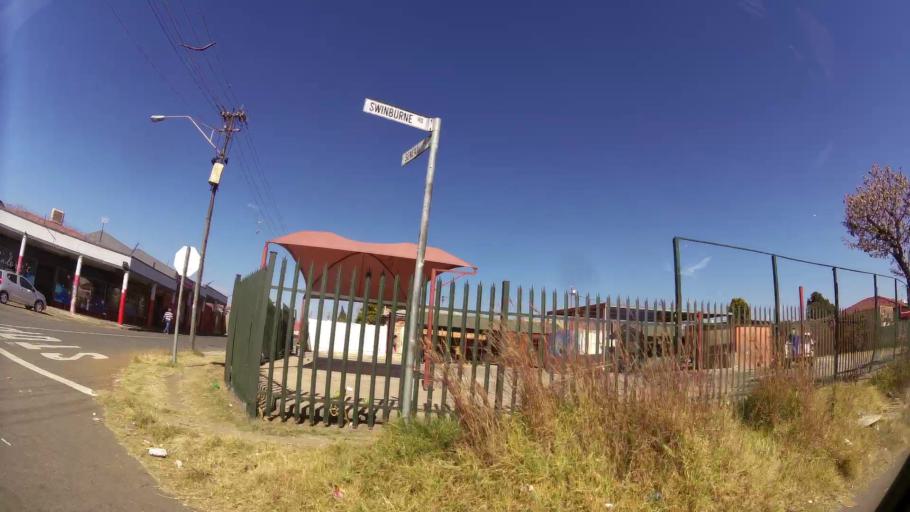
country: ZA
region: Gauteng
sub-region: City of Johannesburg Metropolitan Municipality
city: Johannesburg
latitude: -26.2480
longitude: 28.0876
